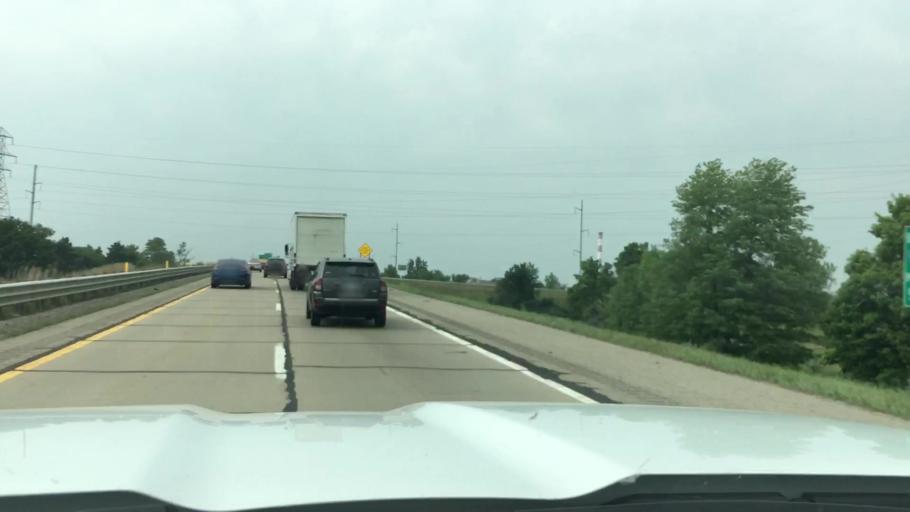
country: US
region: Michigan
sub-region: Eaton County
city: Dimondale
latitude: 42.6752
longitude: -84.6493
